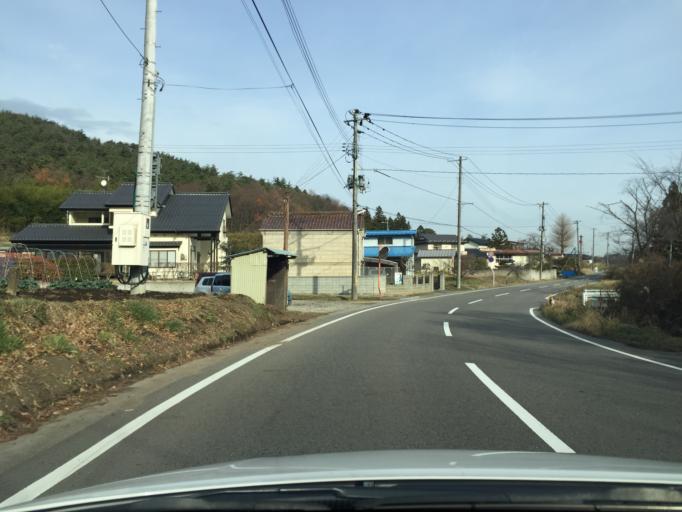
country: JP
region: Fukushima
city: Nihommatsu
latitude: 37.6619
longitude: 140.4428
